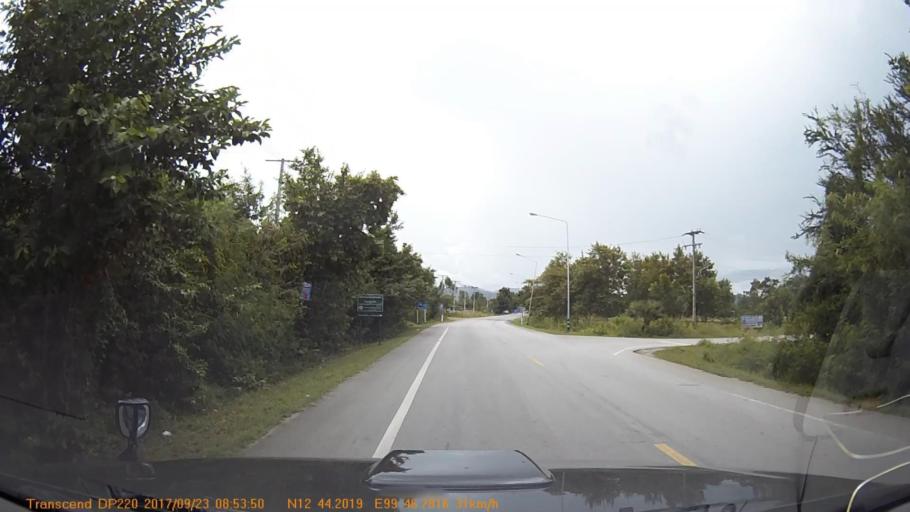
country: TH
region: Phetchaburi
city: Cha-am
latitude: 12.7366
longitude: 99.7799
